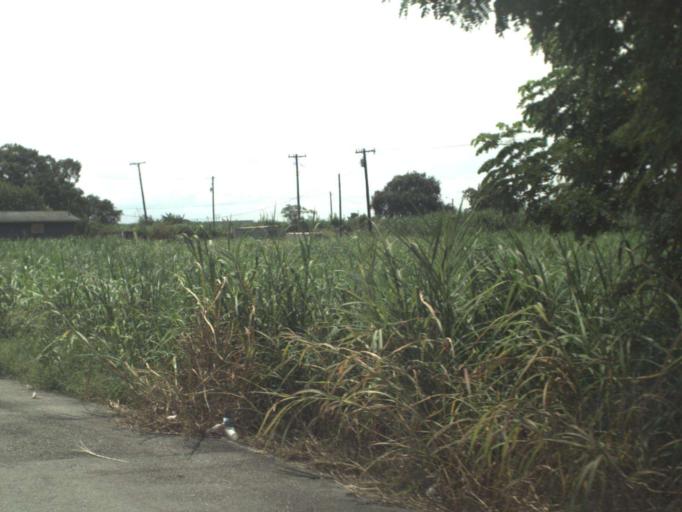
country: US
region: Florida
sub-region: Palm Beach County
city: Pahokee
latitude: 26.8072
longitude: -80.6534
